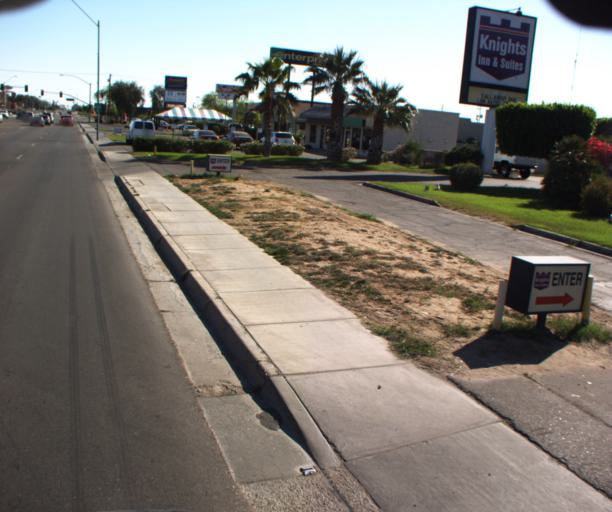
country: US
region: Arizona
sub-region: Yuma County
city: Yuma
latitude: 32.6780
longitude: -114.6246
